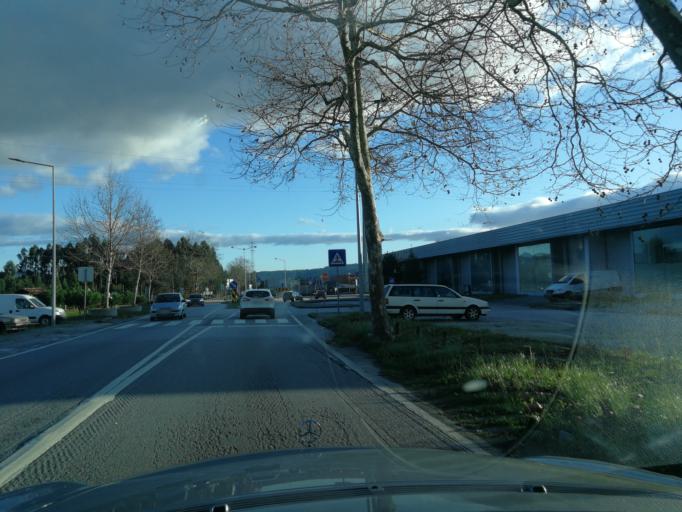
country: PT
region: Viana do Castelo
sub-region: Viana do Castelo
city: Darque
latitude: 41.6338
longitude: -8.7640
